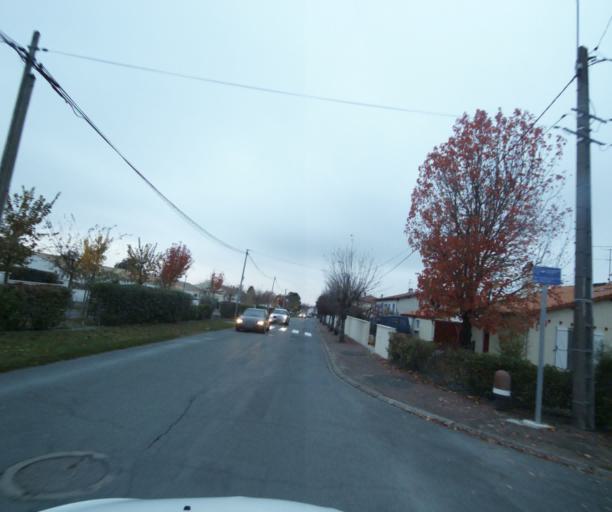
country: FR
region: Poitou-Charentes
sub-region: Departement de la Charente-Maritime
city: Les Gonds
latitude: 45.7406
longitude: -0.6044
